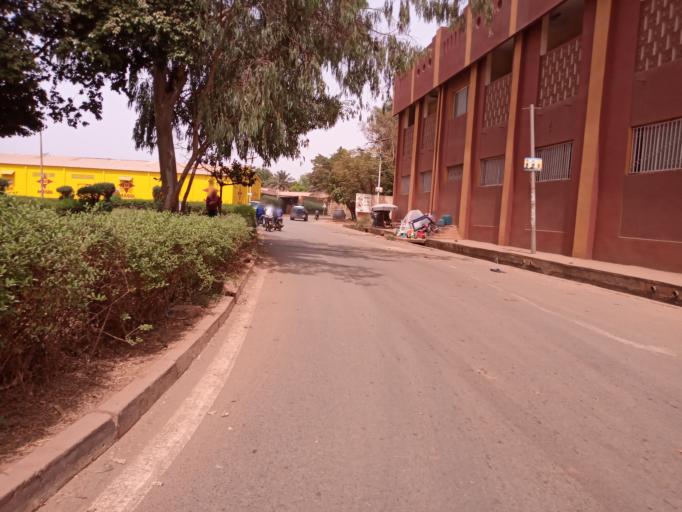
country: ML
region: Bamako
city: Bamako
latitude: 12.6433
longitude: -7.9787
